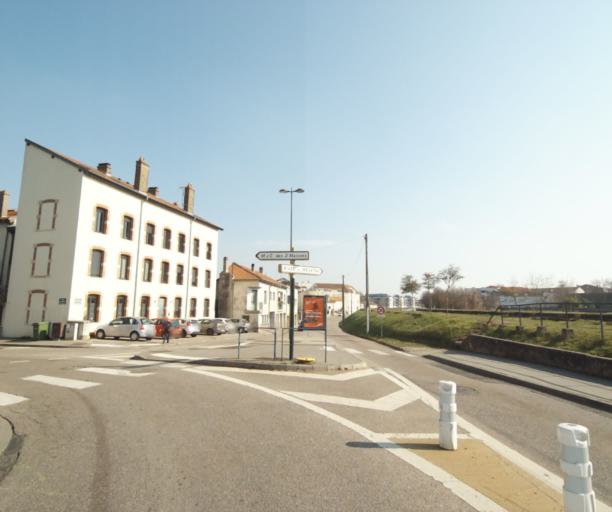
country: FR
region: Lorraine
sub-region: Departement de Meurthe-et-Moselle
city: Maxeville
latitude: 48.7045
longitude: 6.1760
